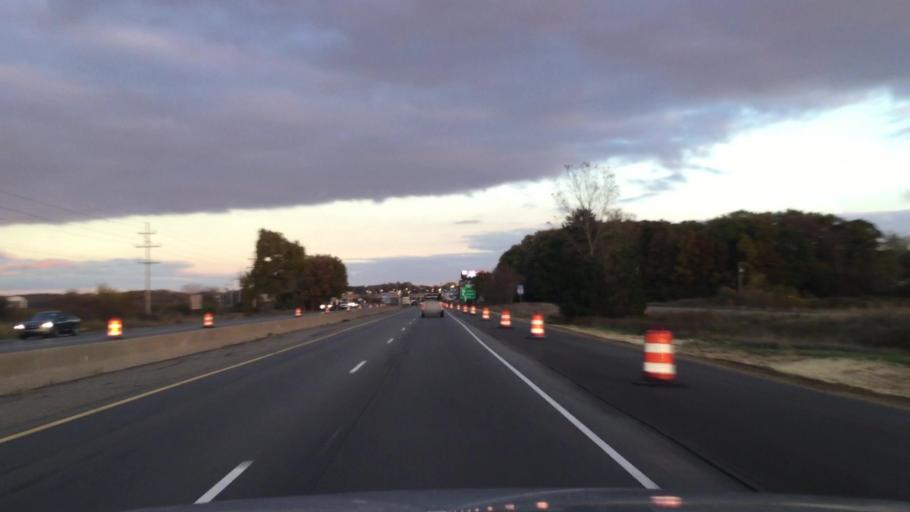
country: US
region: Michigan
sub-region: Jackson County
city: Jackson
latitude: 42.2689
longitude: -84.4456
